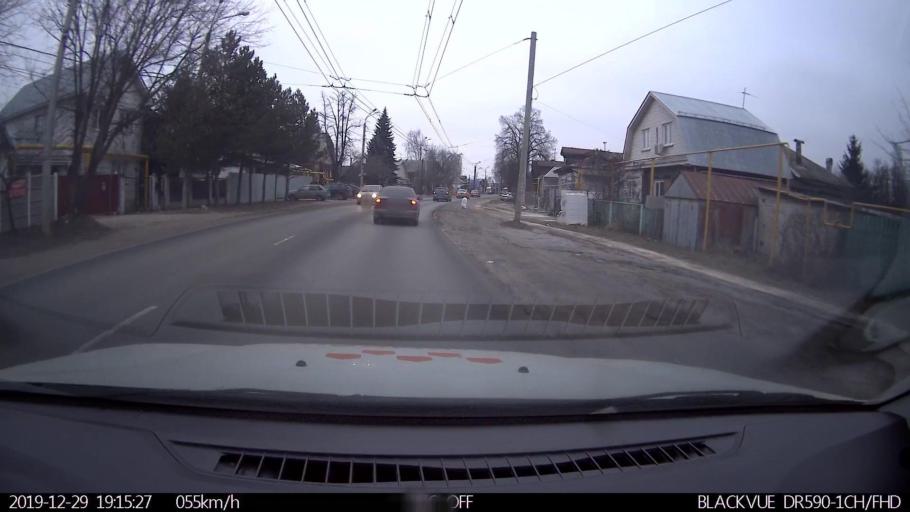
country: RU
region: Nizjnij Novgorod
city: Neklyudovo
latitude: 56.3734
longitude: 43.8368
